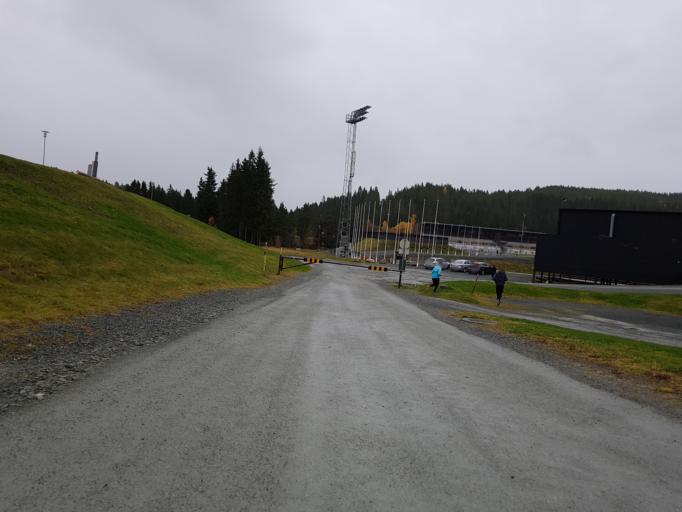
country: NO
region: Sor-Trondelag
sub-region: Melhus
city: Melhus
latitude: 63.3784
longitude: 10.3079
